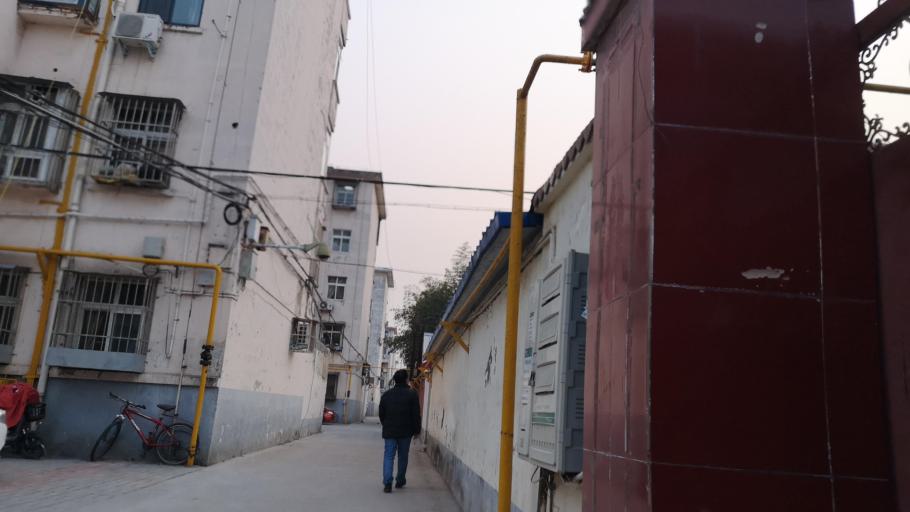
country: CN
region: Henan Sheng
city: Zhongyuanlu
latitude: 35.7821
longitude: 115.0742
